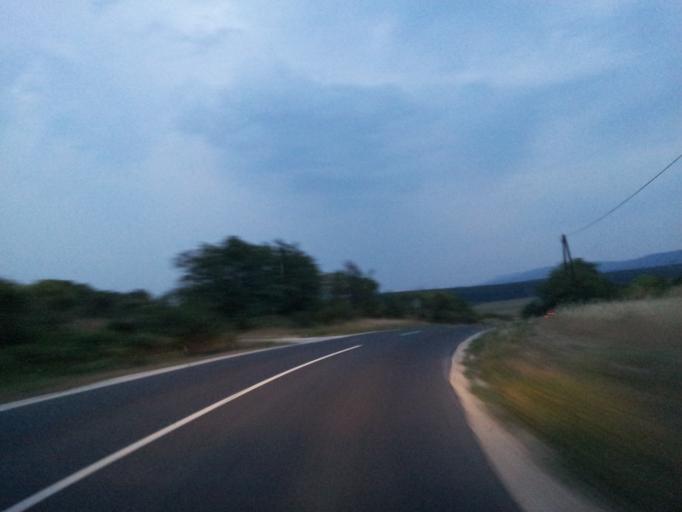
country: HU
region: Veszprem
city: Sumeg
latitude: 46.9749
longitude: 17.3013
